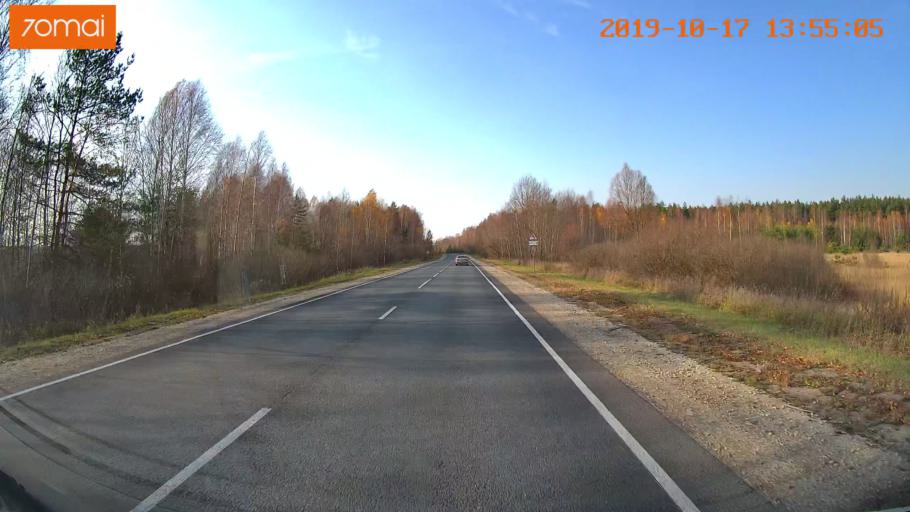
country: RU
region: Rjazan
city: Spas-Klepiki
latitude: 55.1502
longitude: 40.2979
